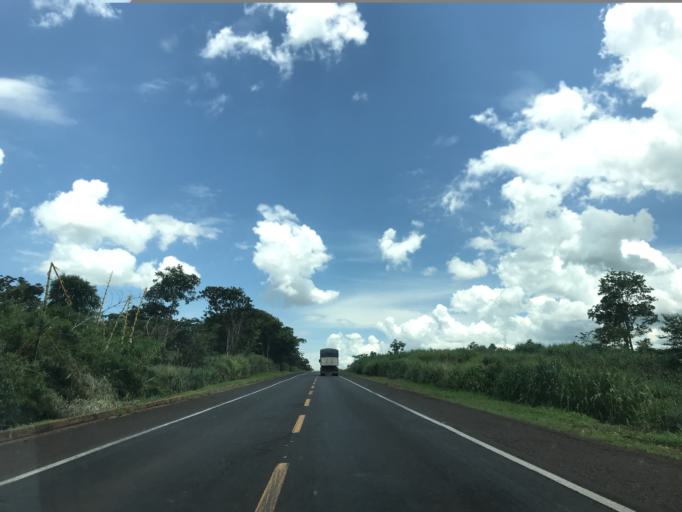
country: BR
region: Minas Gerais
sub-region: Prata
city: Prata
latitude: -19.5044
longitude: -48.8482
